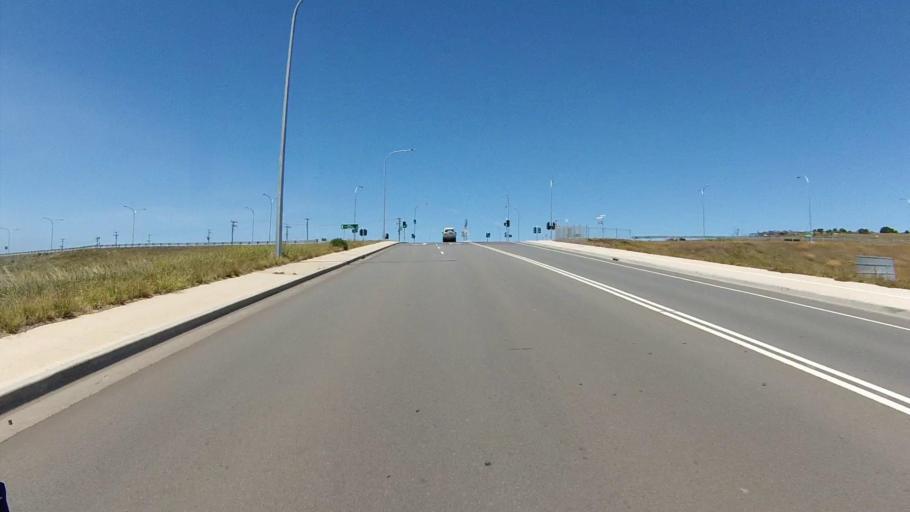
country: AU
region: Tasmania
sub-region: Clarence
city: Howrah
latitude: -42.8879
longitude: 147.4287
